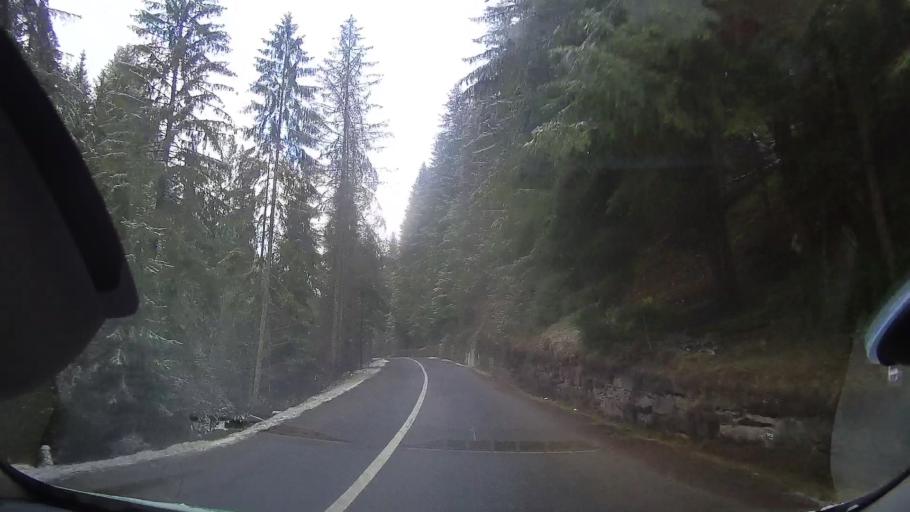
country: RO
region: Alba
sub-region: Comuna Horea
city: Horea
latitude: 46.4883
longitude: 22.9618
